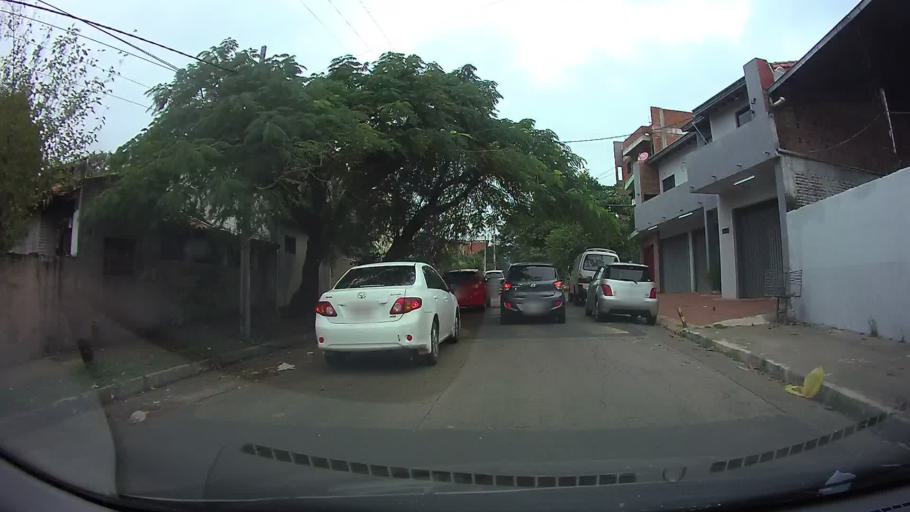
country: PY
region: Asuncion
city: Asuncion
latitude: -25.3146
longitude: -57.6221
